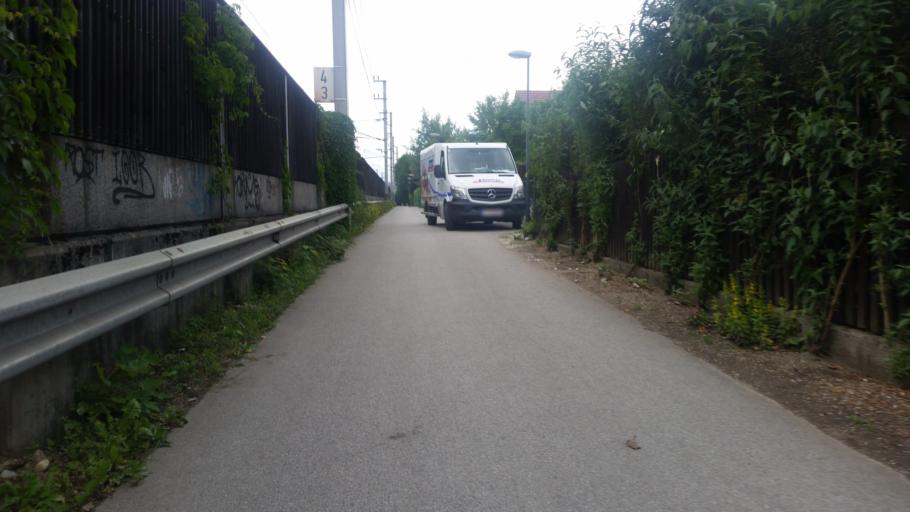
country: AT
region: Salzburg
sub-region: Salzburg Stadt
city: Salzburg
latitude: 47.8005
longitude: 13.0725
